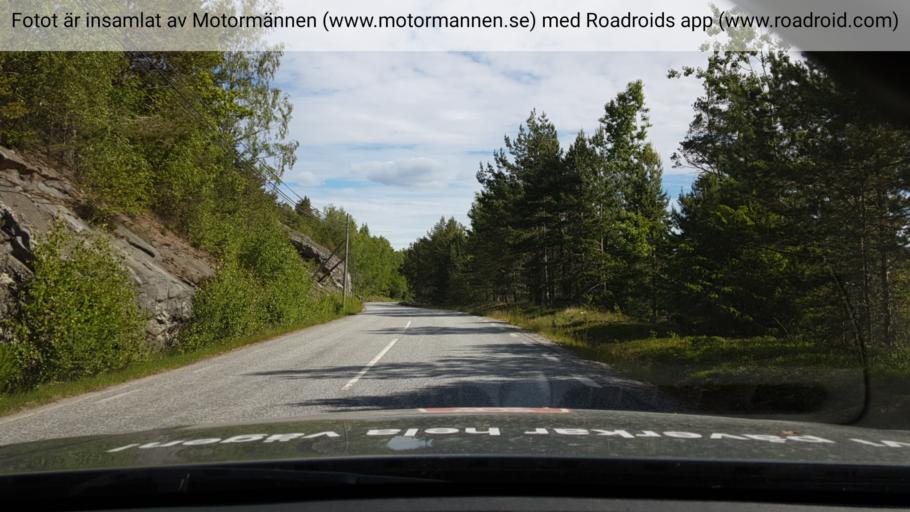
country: SE
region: Stockholm
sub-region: Nynashamns Kommun
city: Nynashamn
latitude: 58.9717
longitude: 18.0679
